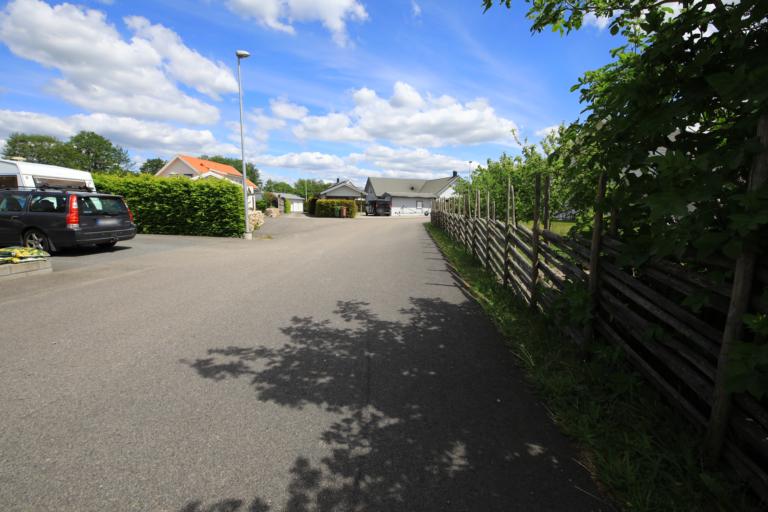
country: SE
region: Halland
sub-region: Varbergs Kommun
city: Varberg
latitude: 57.1561
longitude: 12.2560
